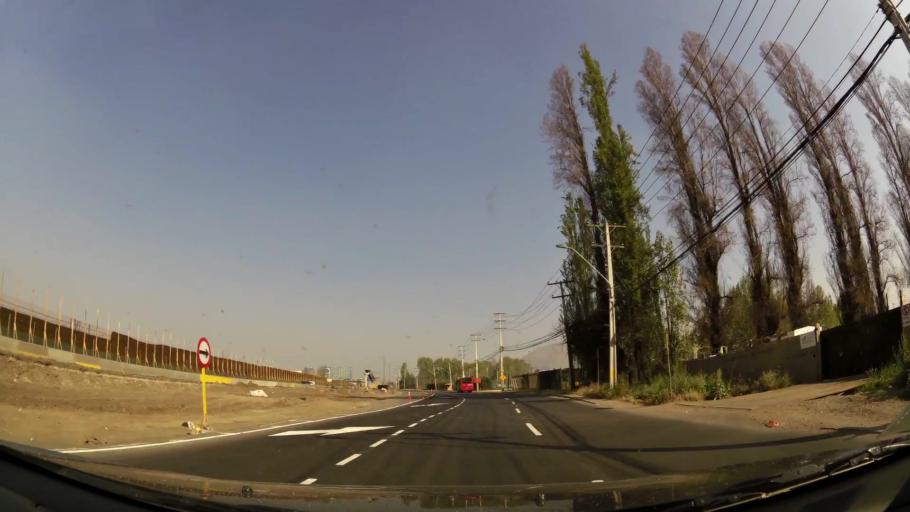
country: CL
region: Santiago Metropolitan
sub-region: Provincia de Santiago
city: Lo Prado
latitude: -33.3577
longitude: -70.7046
